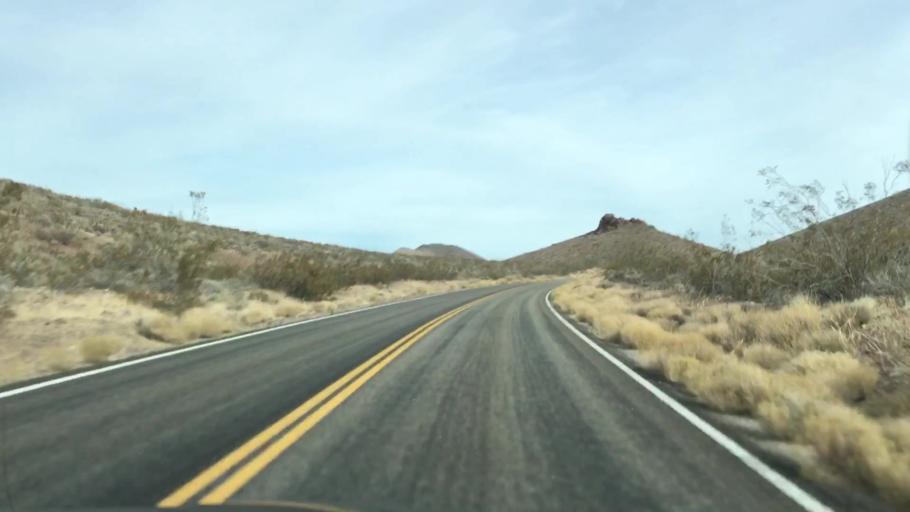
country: US
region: Nevada
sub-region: Nye County
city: Beatty
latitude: 36.7820
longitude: -116.9319
